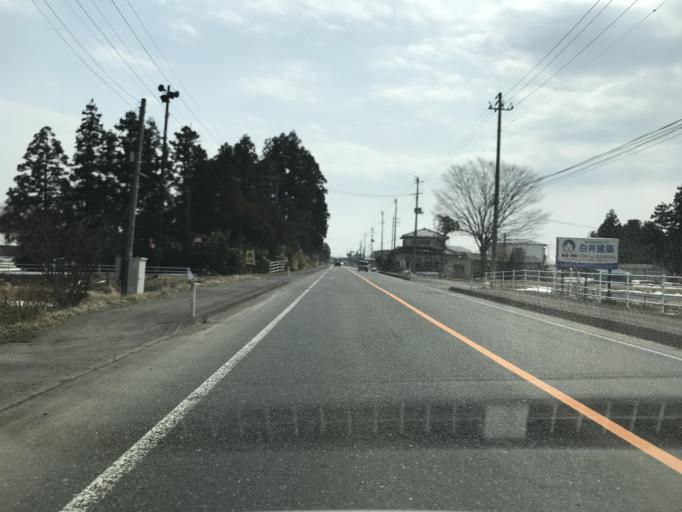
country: JP
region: Miyagi
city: Furukawa
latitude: 38.6873
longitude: 140.8524
